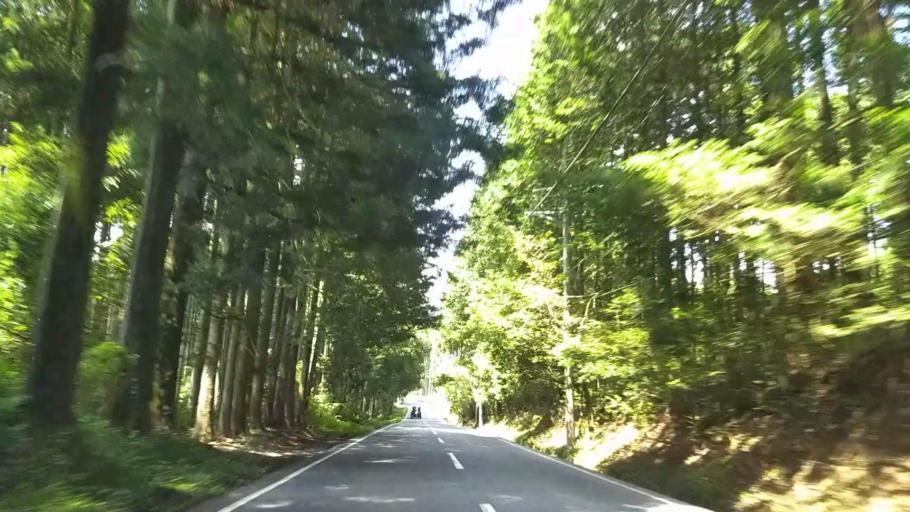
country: JP
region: Shizuoka
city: Fujinomiya
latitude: 35.2910
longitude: 138.6379
